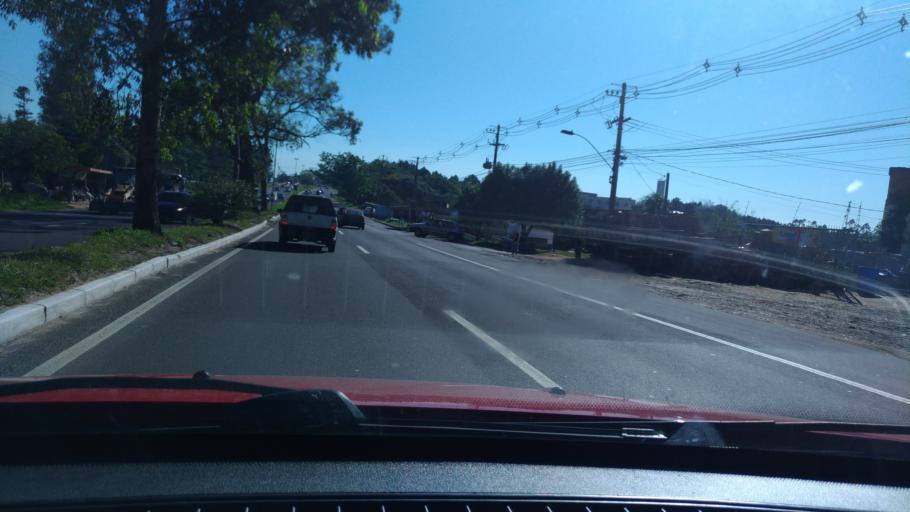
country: BR
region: Rio Grande do Sul
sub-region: Viamao
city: Viamao
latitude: -30.0888
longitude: -51.0603
